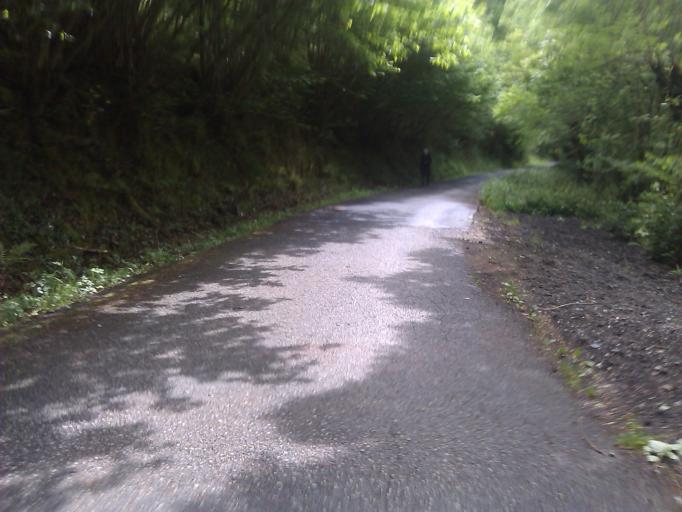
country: ES
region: Navarre
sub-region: Provincia de Navarra
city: Areso
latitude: 43.1041
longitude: -1.9394
